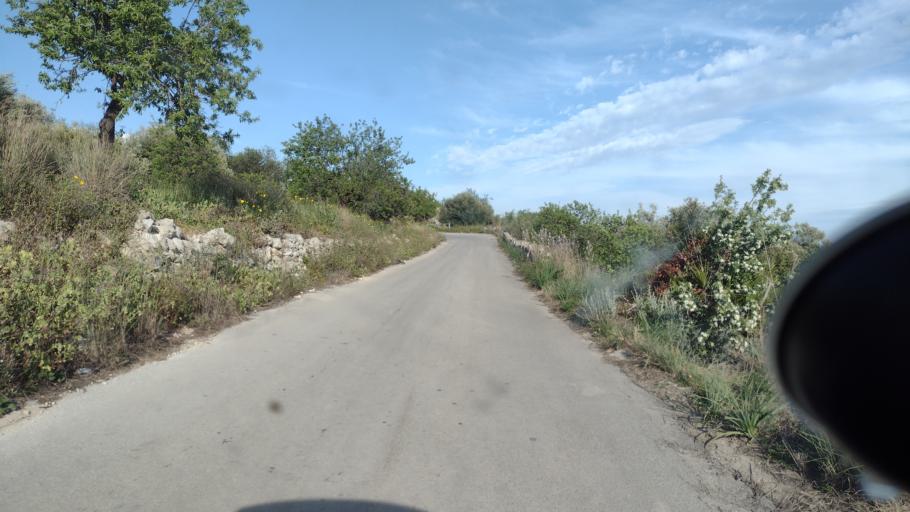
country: IT
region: Sicily
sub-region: Provincia di Siracusa
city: Noto
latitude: 36.8513
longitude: 15.0252
